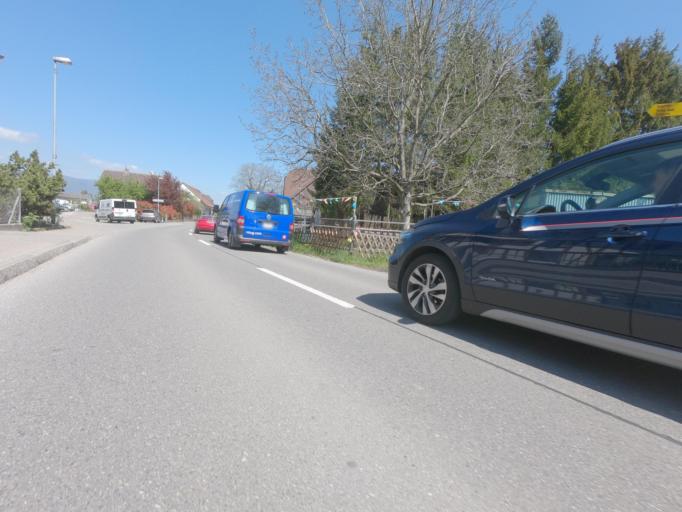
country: CH
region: Bern
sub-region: Biel/Bienne District
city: Orpund
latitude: 47.1278
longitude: 7.3027
